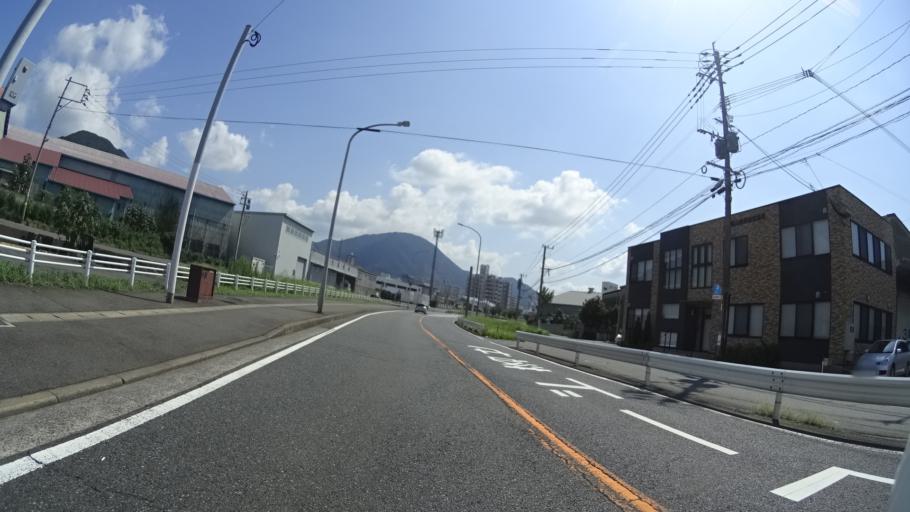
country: JP
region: Yamaguchi
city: Shimonoseki
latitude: 33.9212
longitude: 130.9395
